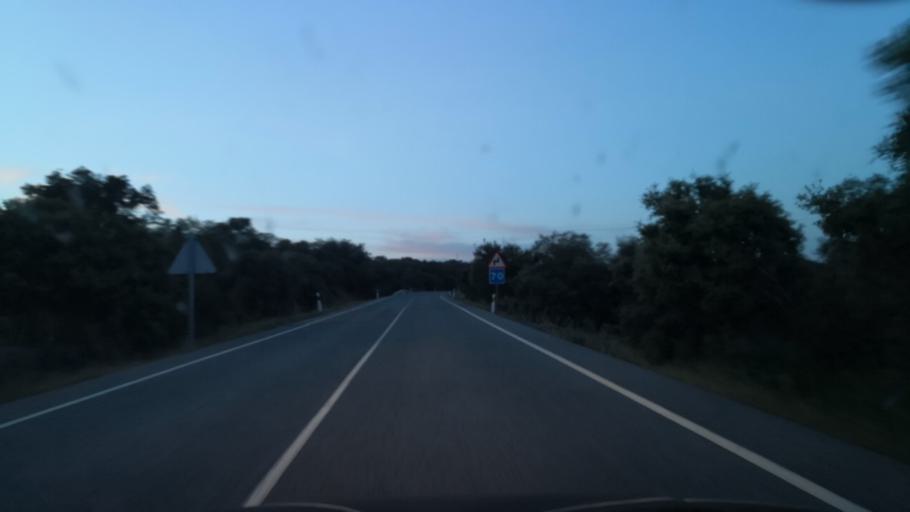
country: ES
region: Extremadura
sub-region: Provincia de Caceres
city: Alcantara
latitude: 39.7399
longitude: -6.9027
